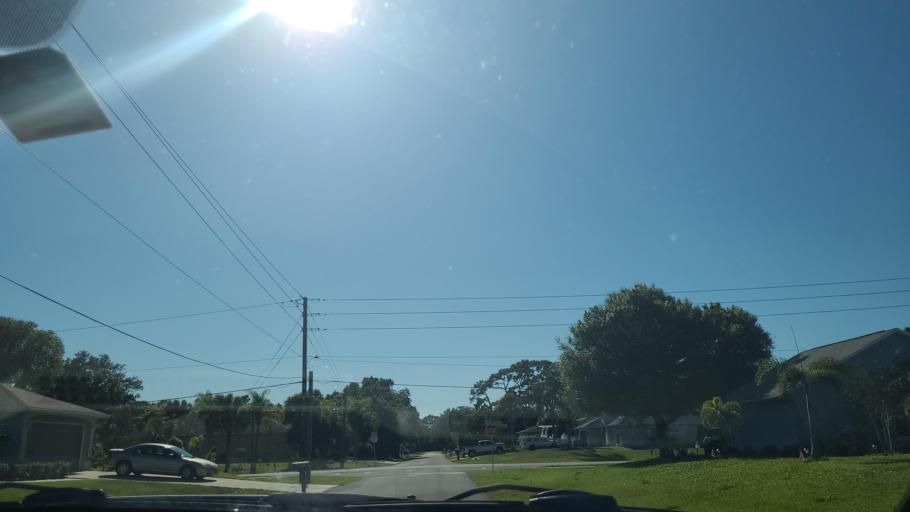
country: US
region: Florida
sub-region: Indian River County
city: Sebastian
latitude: 27.7673
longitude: -80.4970
